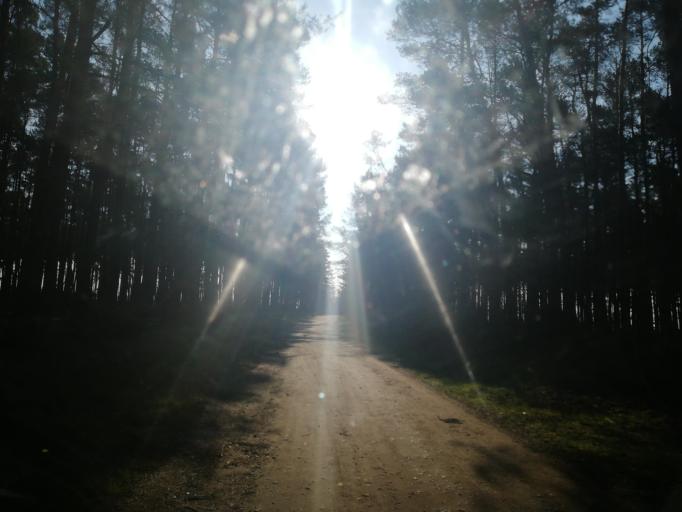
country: DE
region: Brandenburg
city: Drahnsdorf
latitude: 51.9417
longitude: 13.5758
